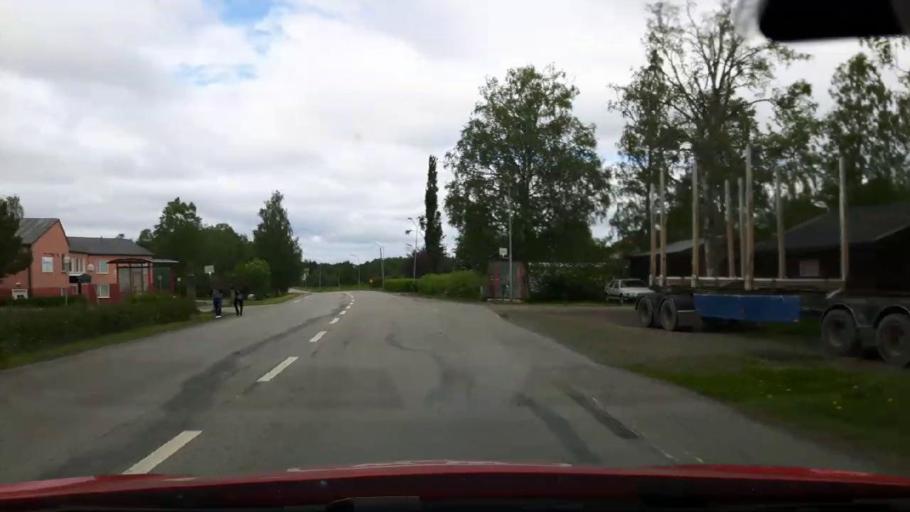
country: SE
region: Jaemtland
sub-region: Krokoms Kommun
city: Krokom
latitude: 63.3042
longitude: 14.4703
